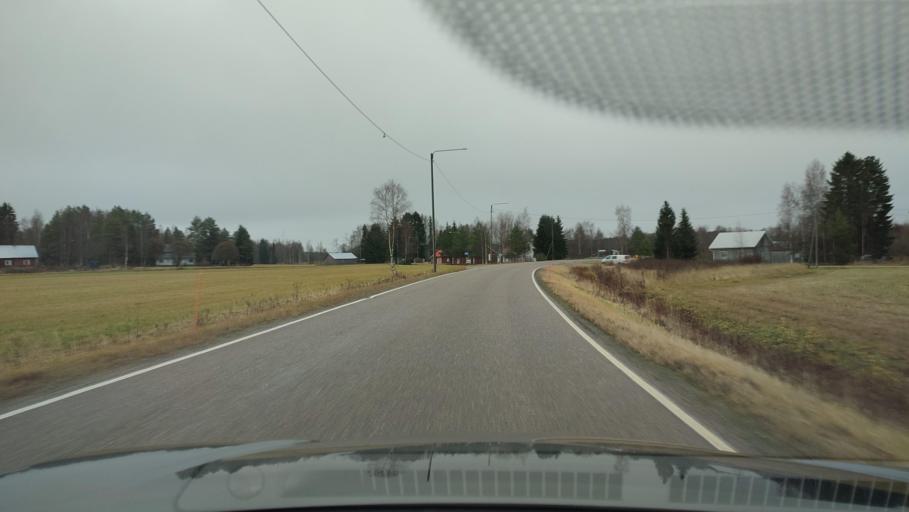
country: FI
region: Southern Ostrobothnia
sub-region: Suupohja
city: Isojoki
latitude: 62.2345
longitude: 22.0216
